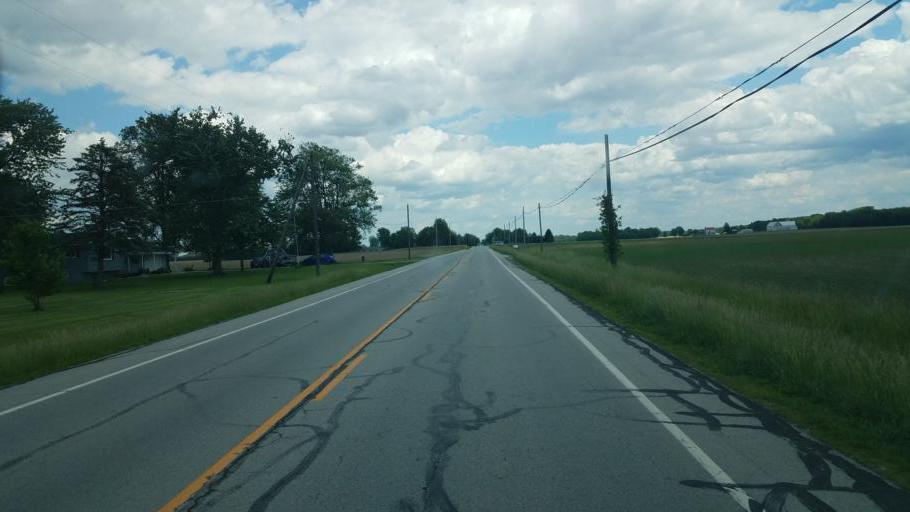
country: US
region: Ohio
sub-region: Crawford County
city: Bucyrus
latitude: 40.8129
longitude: -82.8925
